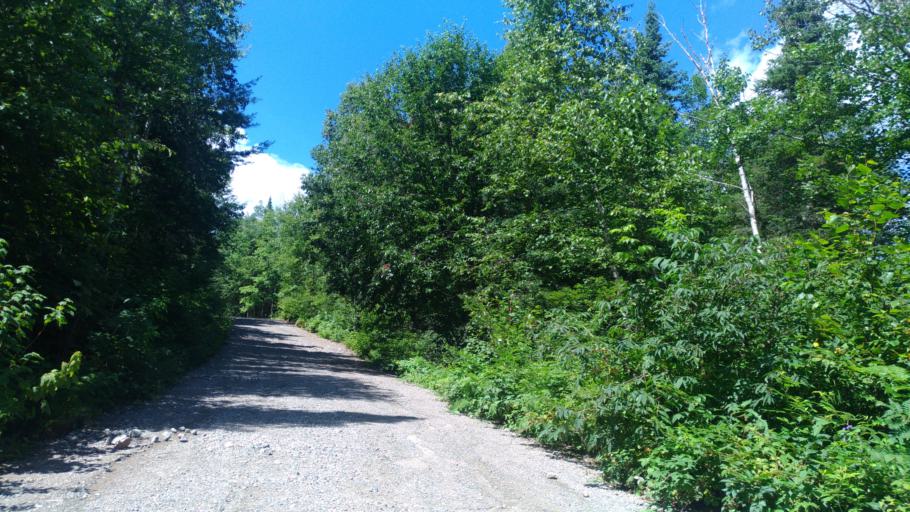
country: CA
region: Ontario
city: Rayside-Balfour
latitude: 46.5922
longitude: -81.5486
